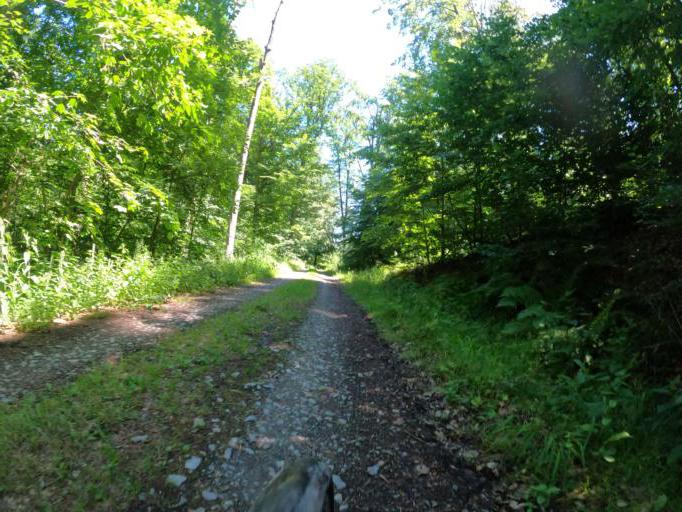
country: DE
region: Baden-Wuerttemberg
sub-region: Regierungsbezirk Stuttgart
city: Sersheim
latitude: 49.0050
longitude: 8.9888
